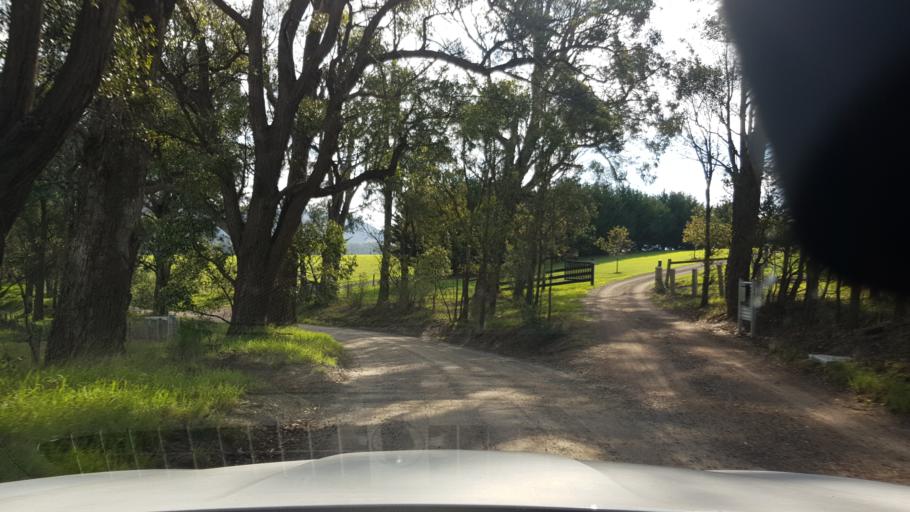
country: AU
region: Victoria
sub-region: East Gippsland
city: Bairnsdale
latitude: -37.7782
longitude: 147.5748
